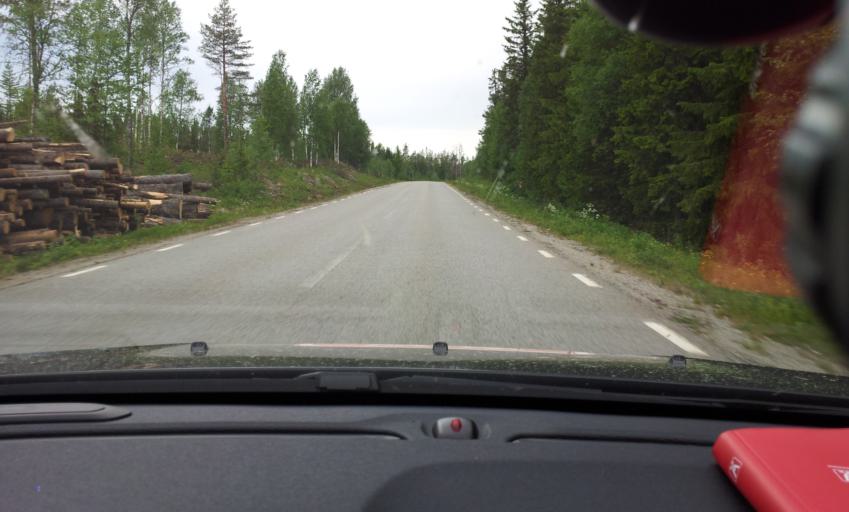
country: SE
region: Jaemtland
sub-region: Bergs Kommun
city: Hoverberg
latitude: 62.6835
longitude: 14.6425
